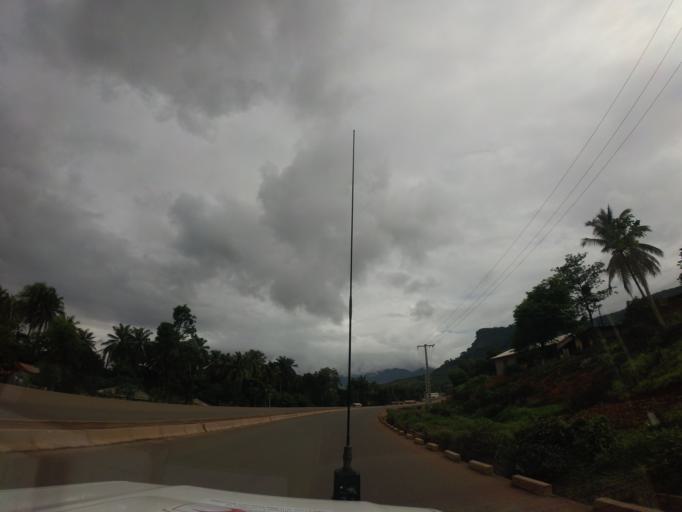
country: GN
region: Kindia
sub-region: Coyah
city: Coyah
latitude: 9.7078
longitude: -13.3990
